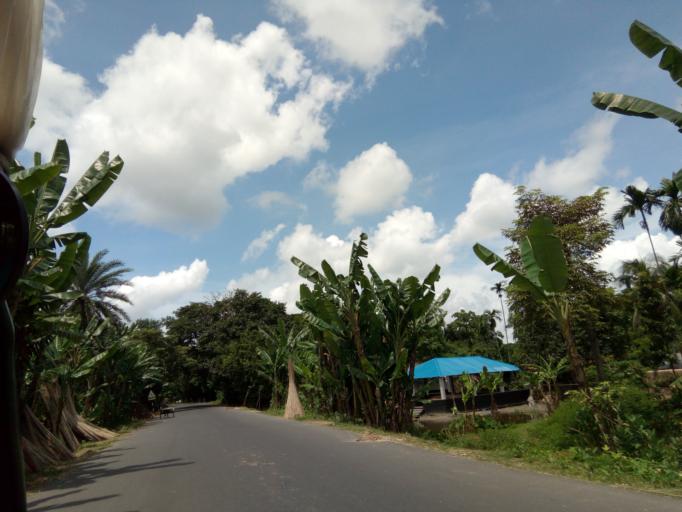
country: BD
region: Dhaka
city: Tungipara
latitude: 22.9092
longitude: 89.8758
